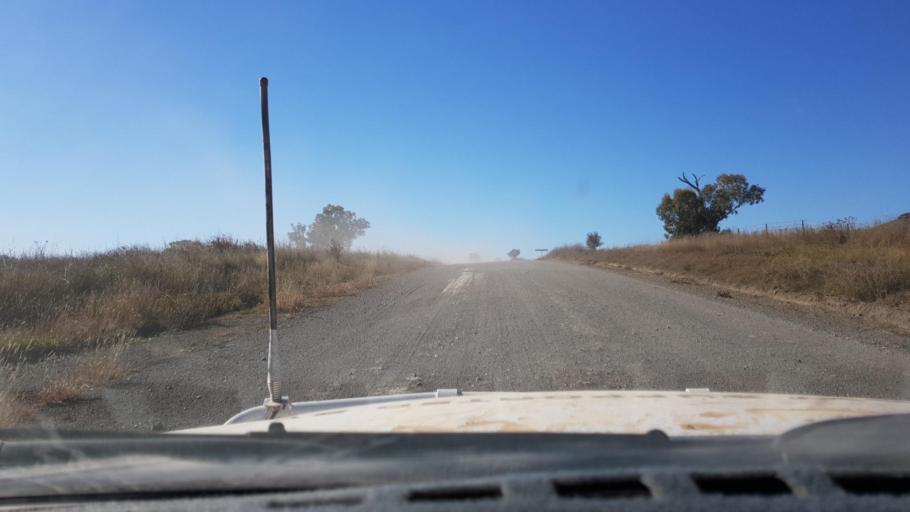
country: AU
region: New South Wales
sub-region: Narrabri
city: Blair Athol
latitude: -30.6752
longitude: 150.4354
